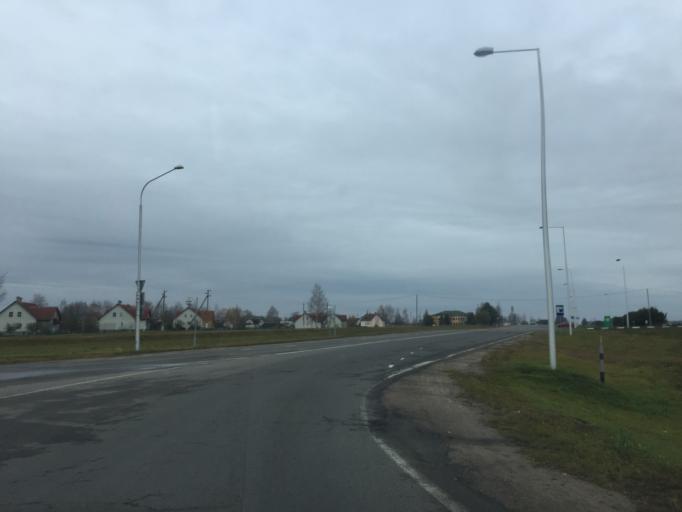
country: BY
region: Mogilev
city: Horki
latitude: 54.3079
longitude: 30.9390
